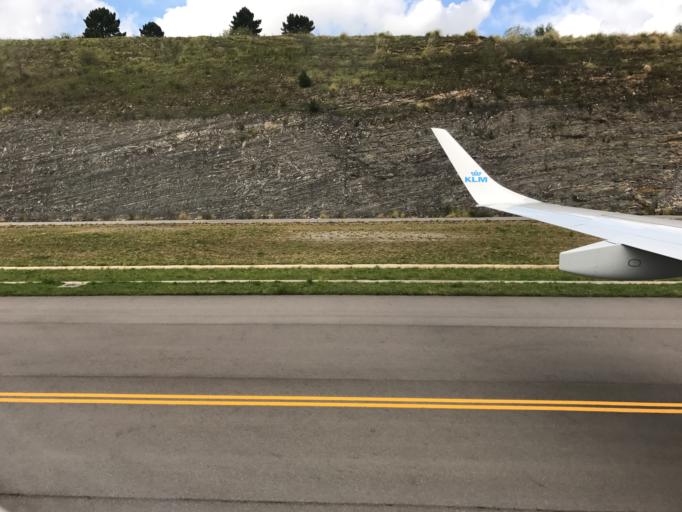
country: ES
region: Basque Country
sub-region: Bizkaia
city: Sondika
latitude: 43.3058
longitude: -2.9182
